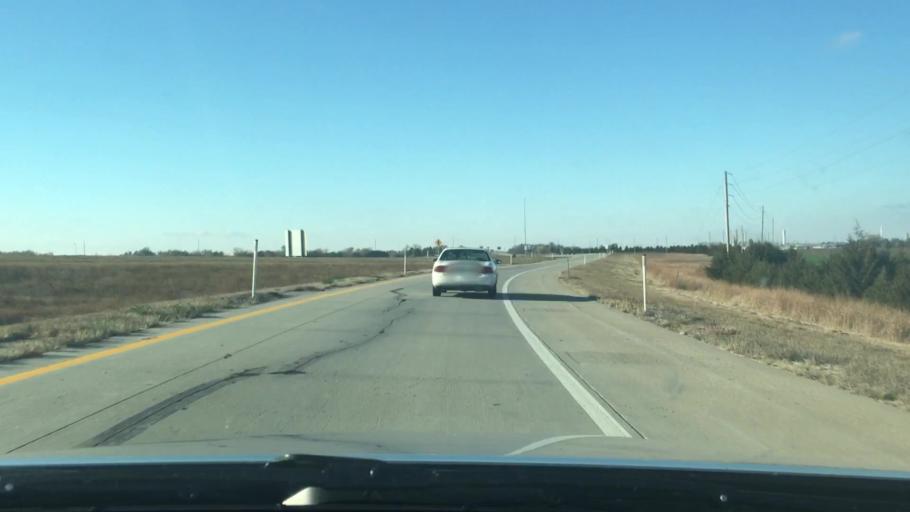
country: US
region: Kansas
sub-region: Reno County
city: South Hutchinson
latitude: 38.0168
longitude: -97.9674
